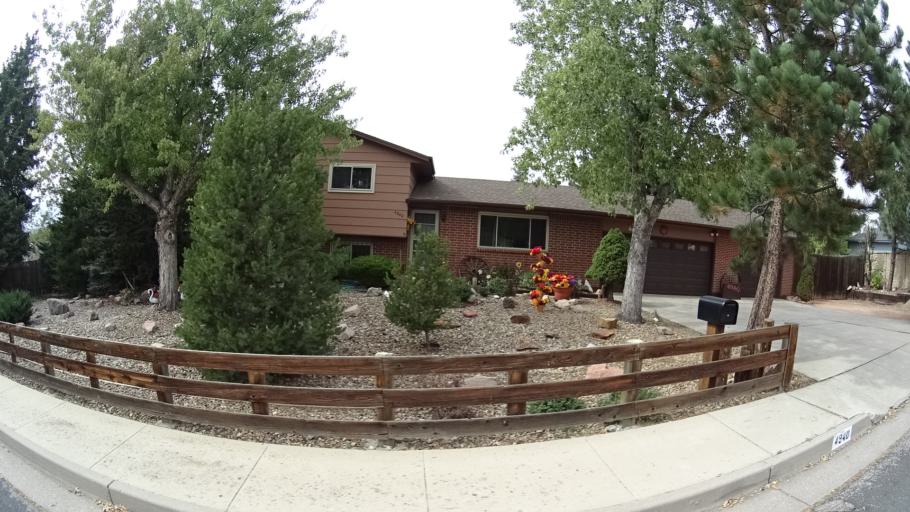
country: US
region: Colorado
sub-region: El Paso County
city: Cimarron Hills
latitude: 38.8986
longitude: -104.7360
